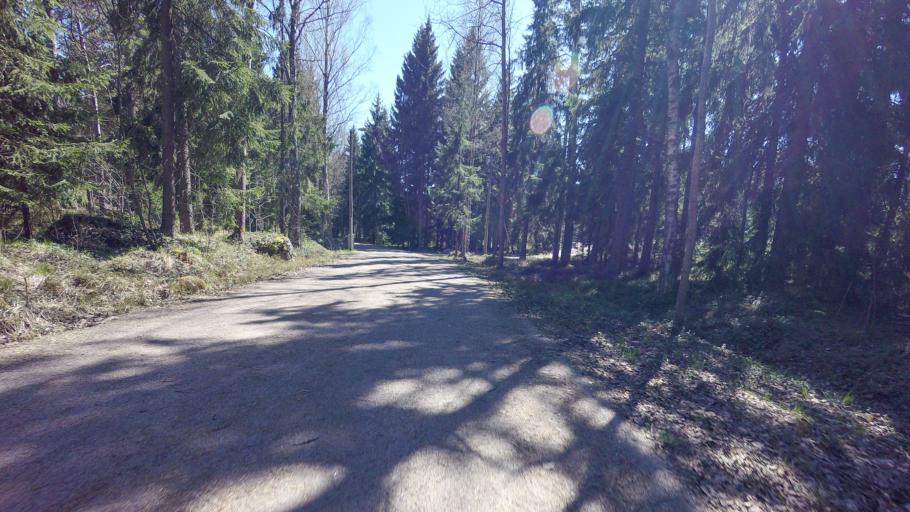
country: FI
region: Uusimaa
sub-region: Helsinki
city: Vantaa
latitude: 60.2315
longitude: 25.1426
